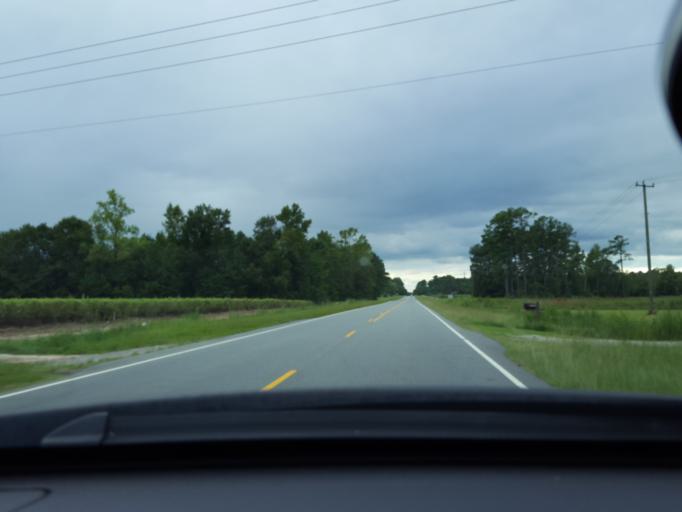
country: US
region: North Carolina
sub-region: Bladen County
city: Elizabethtown
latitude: 34.7375
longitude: -78.4308
